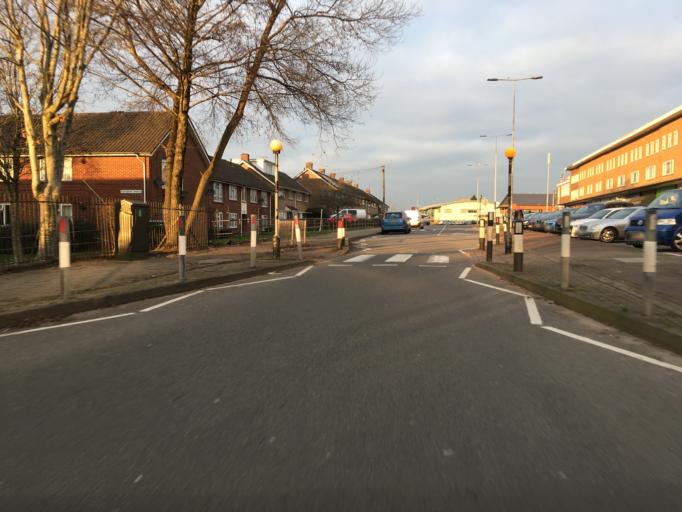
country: GB
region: Wales
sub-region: Newport
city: Marshfield
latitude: 51.5204
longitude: -3.1203
